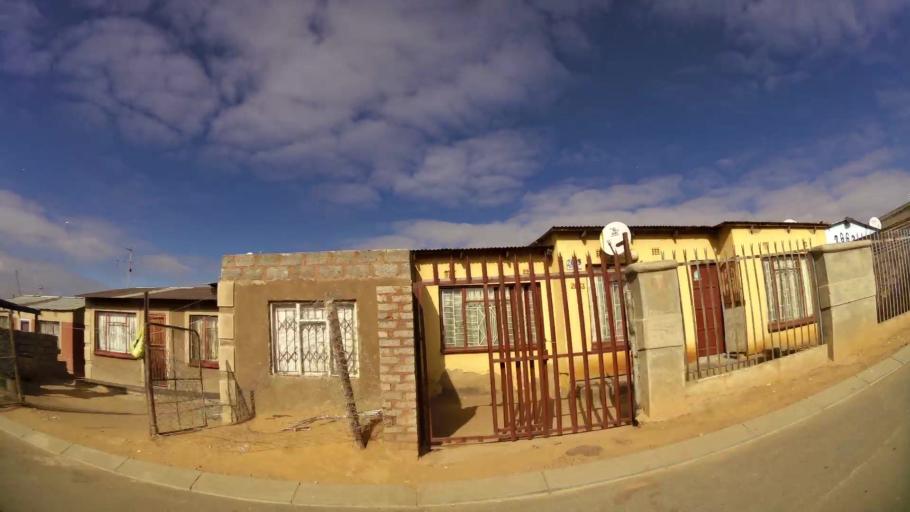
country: ZA
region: Gauteng
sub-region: City of Johannesburg Metropolitan Municipality
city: Modderfontein
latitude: -26.0534
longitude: 28.1812
